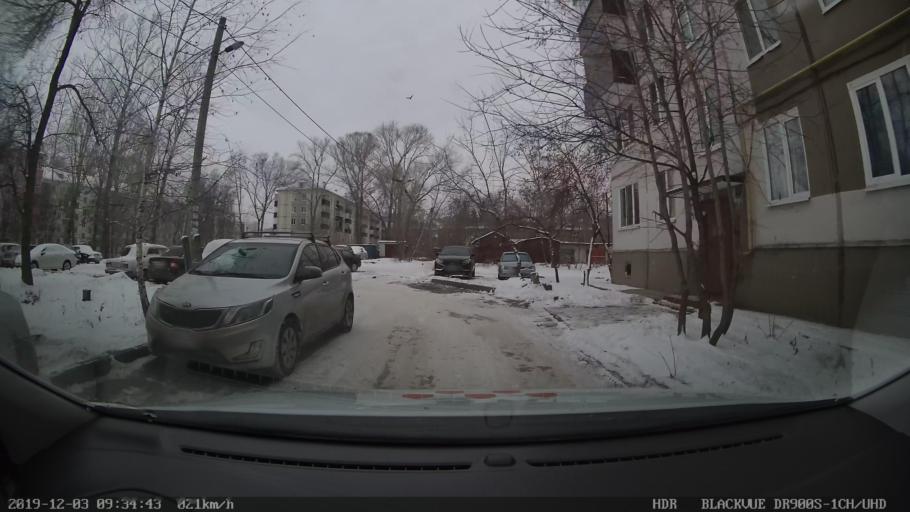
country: RU
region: Tatarstan
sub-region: Gorod Kazan'
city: Kazan
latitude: 55.7743
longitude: 49.1109
